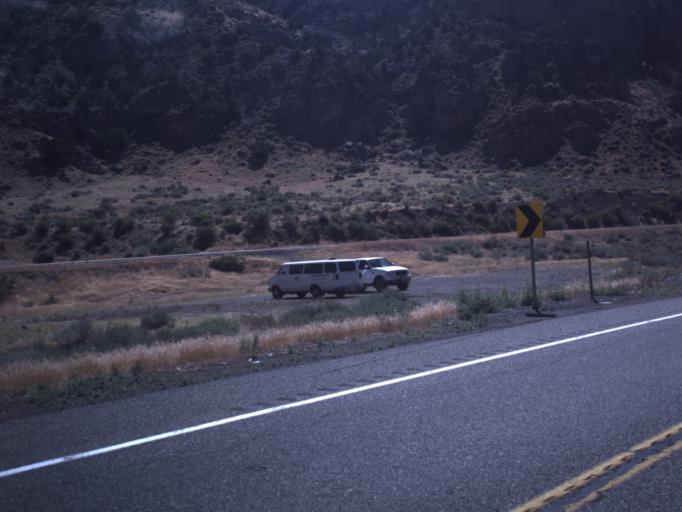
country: US
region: Utah
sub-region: Sevier County
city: Monroe
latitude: 38.5705
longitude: -112.2532
